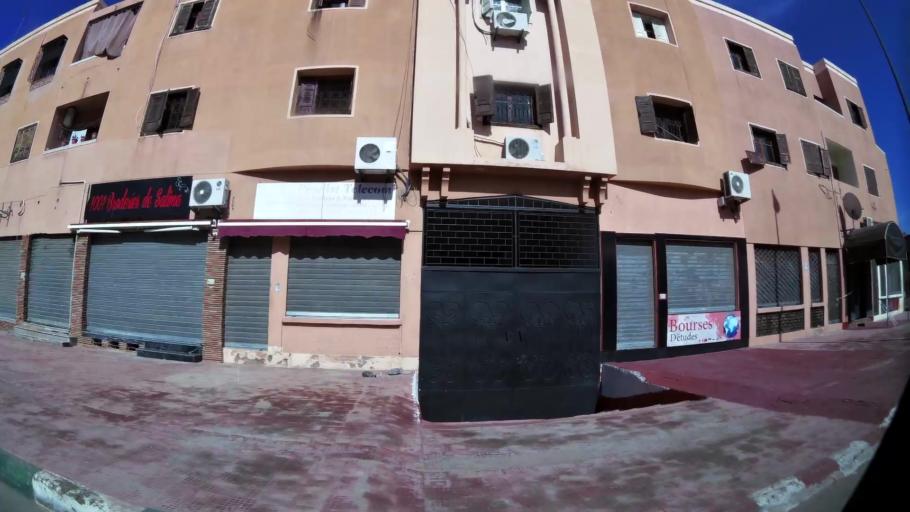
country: MA
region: Marrakech-Tensift-Al Haouz
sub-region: Marrakech
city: Marrakesh
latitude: 31.6527
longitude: -8.0145
